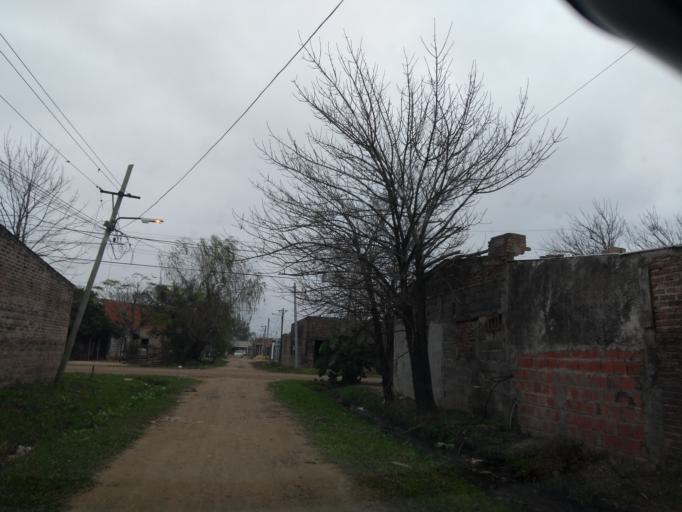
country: AR
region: Chaco
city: Resistencia
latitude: -27.4774
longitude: -58.9776
